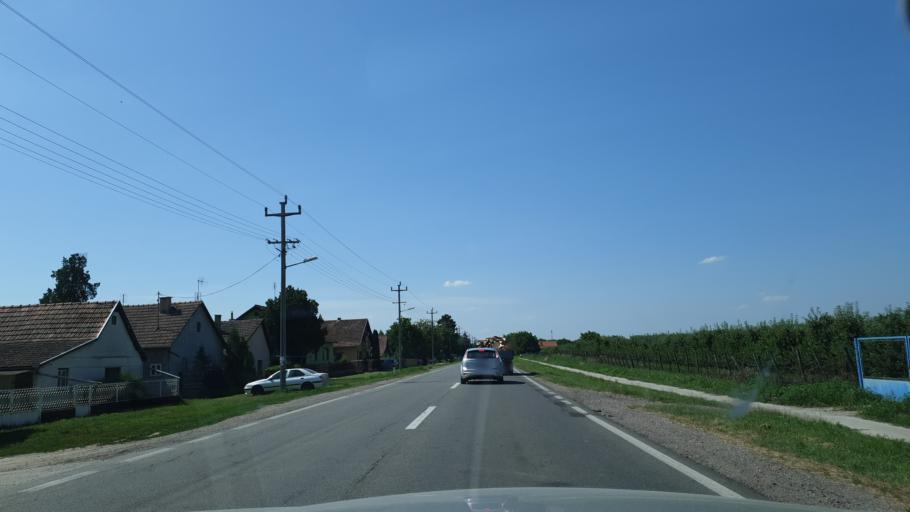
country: HU
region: Bacs-Kiskun
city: Kelebia
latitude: 46.1400
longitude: 19.5913
